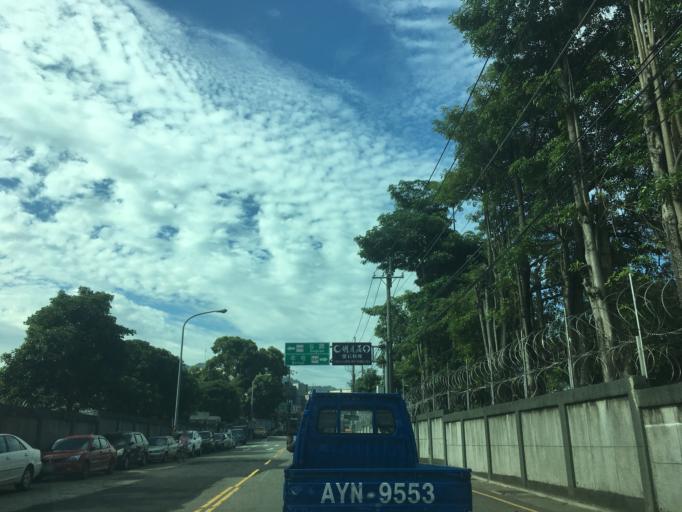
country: TW
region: Taiwan
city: Fengyuan
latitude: 24.2069
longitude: 120.7944
